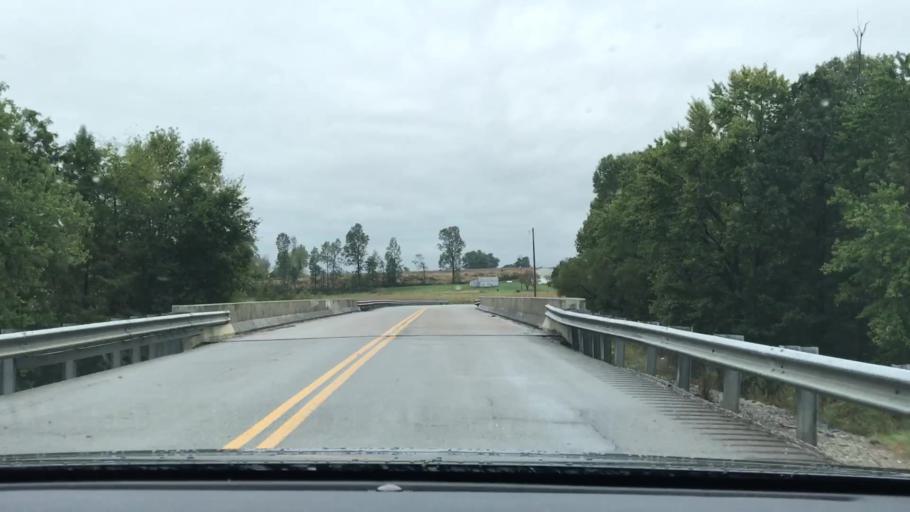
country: US
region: Kentucky
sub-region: McLean County
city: Calhoun
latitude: 37.4905
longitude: -87.2452
